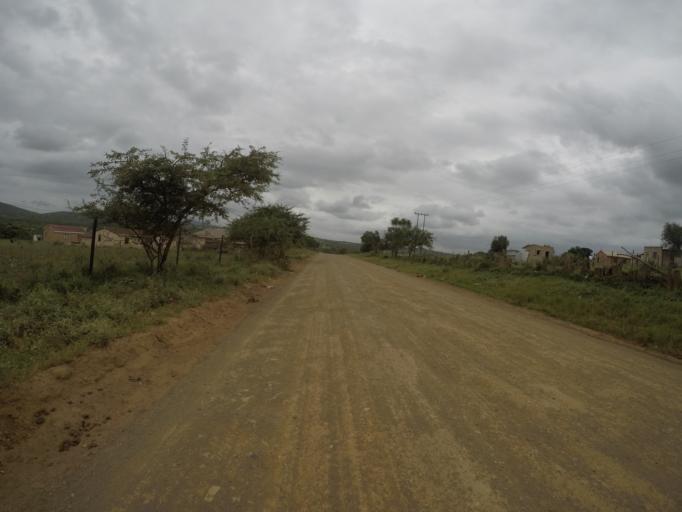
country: ZA
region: KwaZulu-Natal
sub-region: uThungulu District Municipality
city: Empangeni
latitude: -28.5824
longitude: 31.8459
